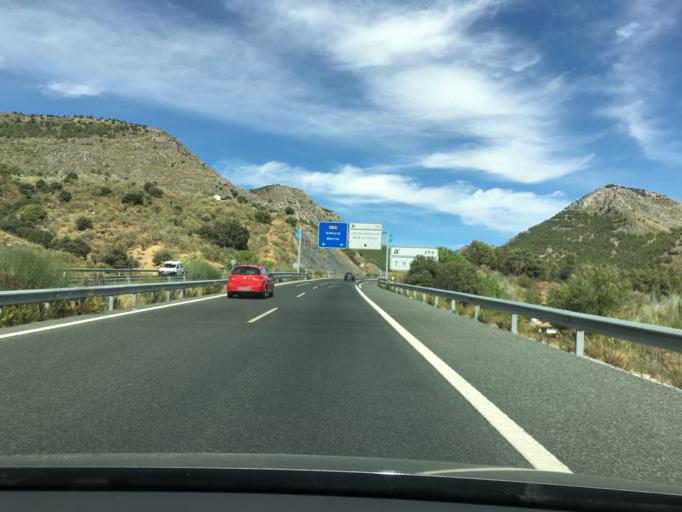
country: ES
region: Andalusia
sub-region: Provincia de Granada
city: Huetor Santillan
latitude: 37.2304
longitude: -3.5015
